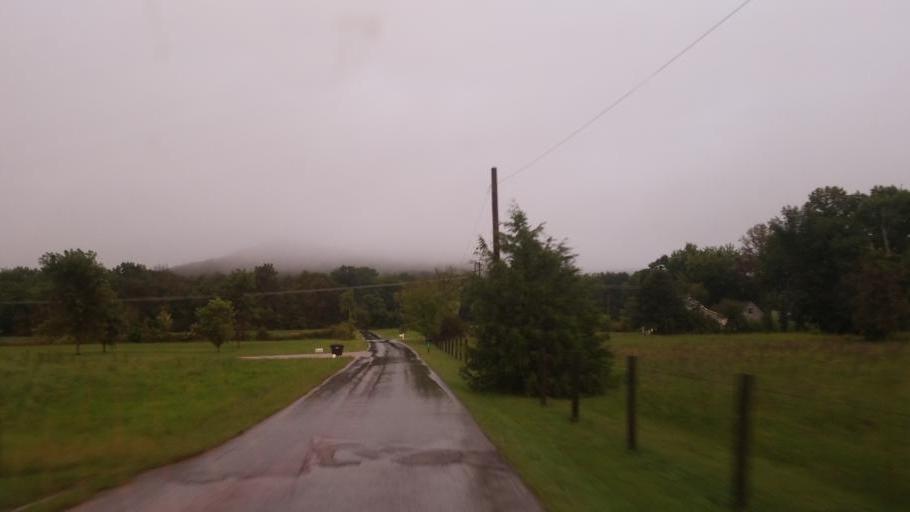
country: US
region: Kentucky
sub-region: Fleming County
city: Flemingsburg
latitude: 38.4497
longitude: -83.6300
